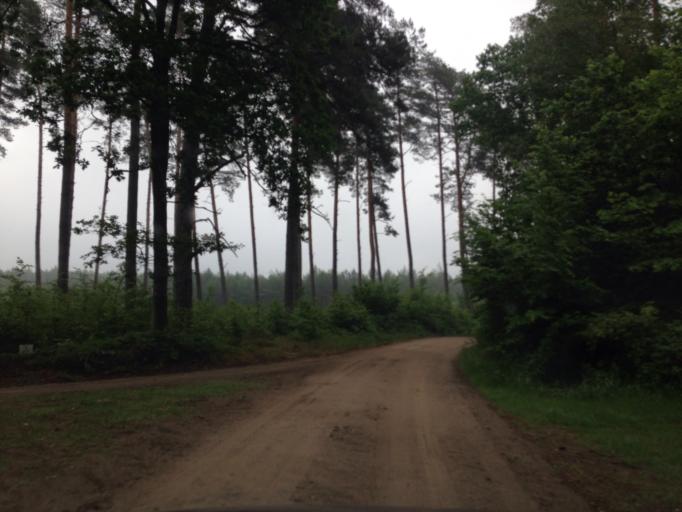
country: PL
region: Kujawsko-Pomorskie
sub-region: Powiat brodnicki
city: Bobrowo
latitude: 53.3638
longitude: 19.3023
